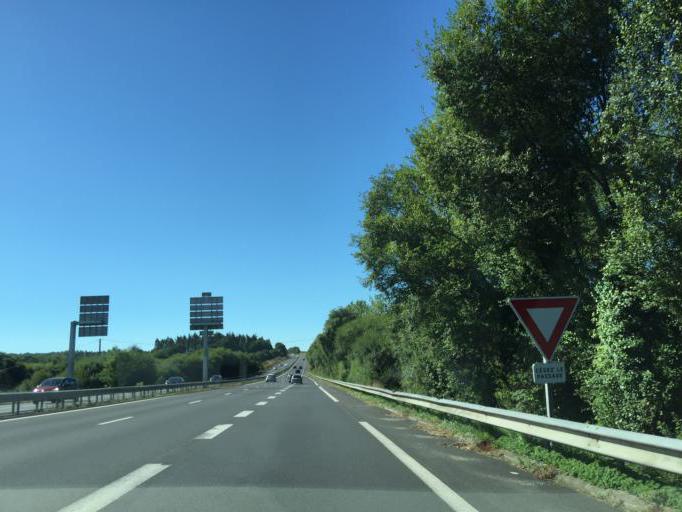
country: FR
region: Brittany
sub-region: Departement des Cotes-d'Armor
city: Saint-Samson-sur-Rance
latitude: 48.5184
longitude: -2.0386
